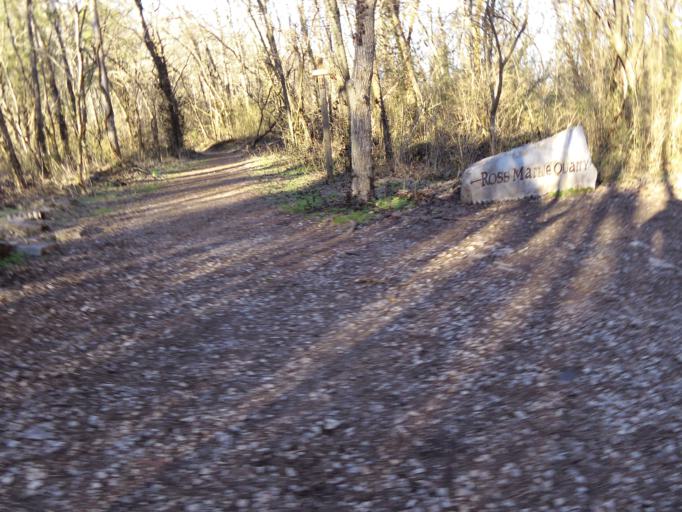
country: US
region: Tennessee
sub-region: Knox County
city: Knoxville
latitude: 35.9482
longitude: -83.8711
